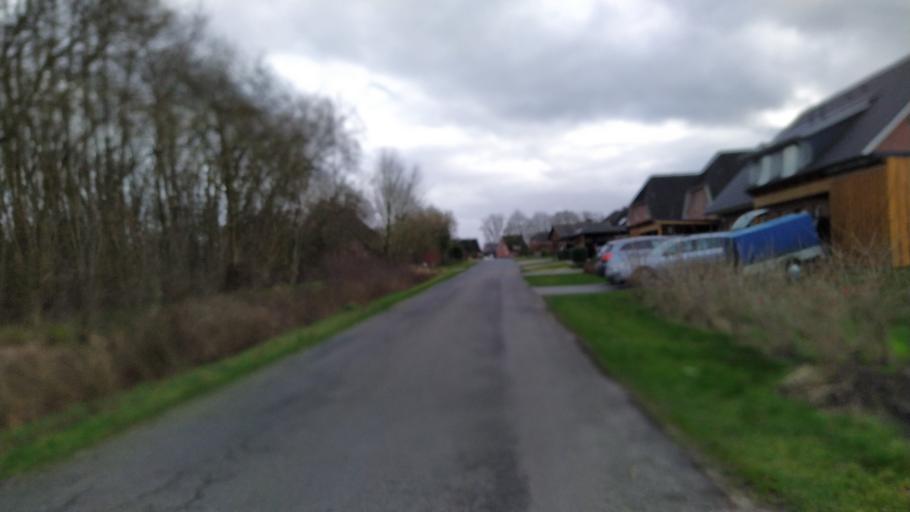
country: DE
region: Lower Saxony
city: Bargstedt
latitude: 53.4397
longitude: 9.4677
